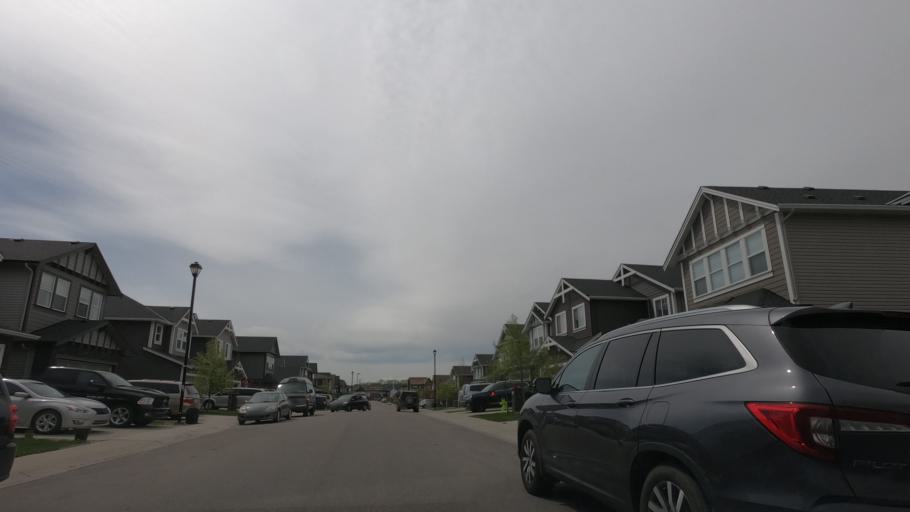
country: CA
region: Alberta
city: Airdrie
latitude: 51.3046
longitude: -114.0354
